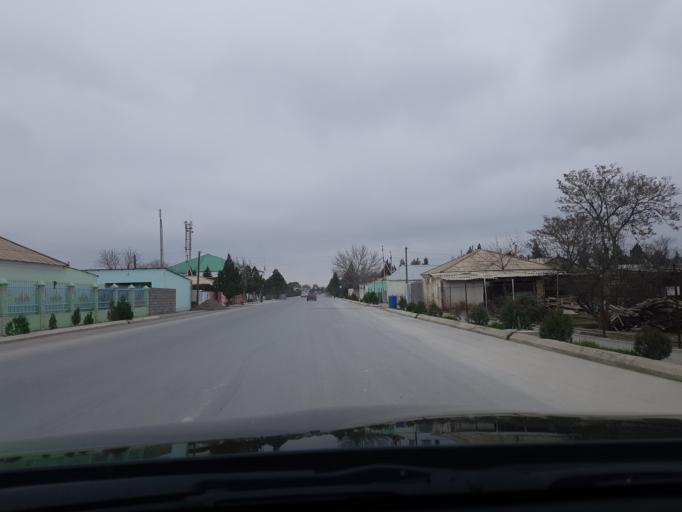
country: TM
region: Ahal
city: Abadan
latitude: 38.1519
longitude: 57.9586
